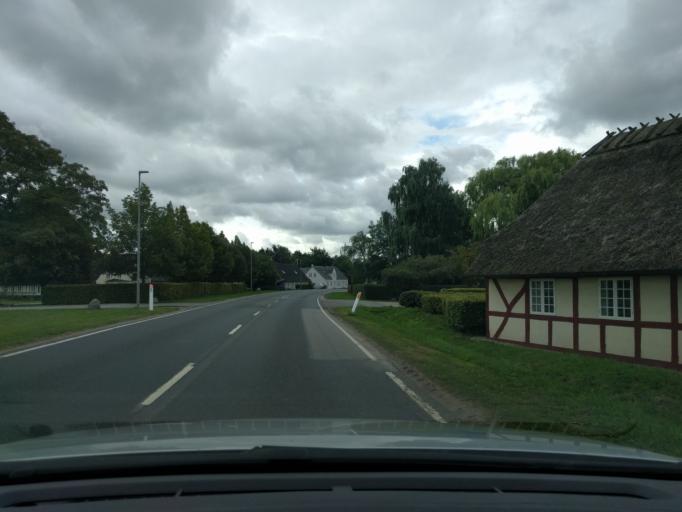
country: DK
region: South Denmark
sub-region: Nyborg Kommune
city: Ullerslev
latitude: 55.3840
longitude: 10.6675
